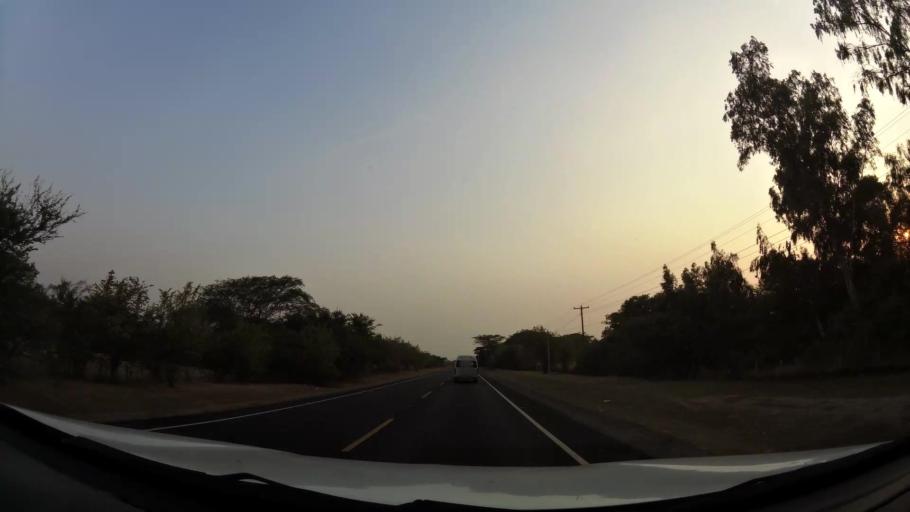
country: NI
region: Leon
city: La Paz Centro
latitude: 12.3052
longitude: -86.7069
